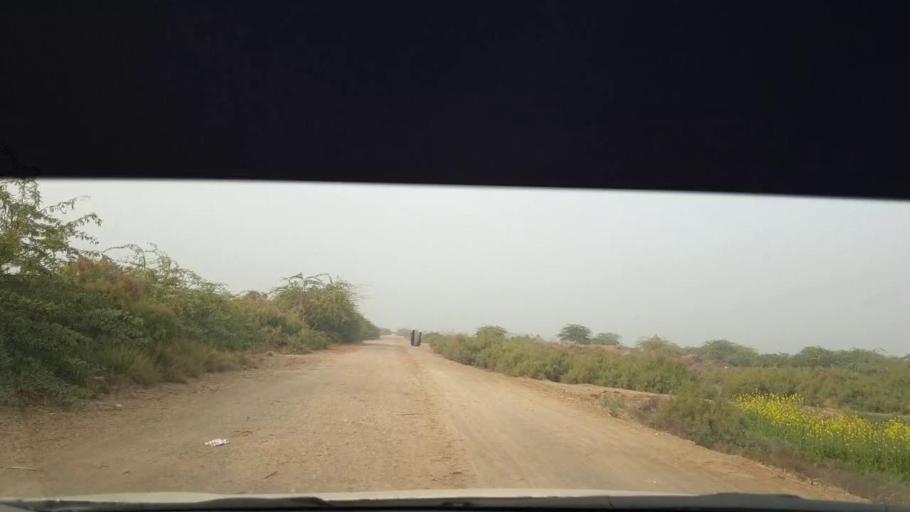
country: PK
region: Sindh
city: Berani
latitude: 25.8065
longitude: 68.8822
